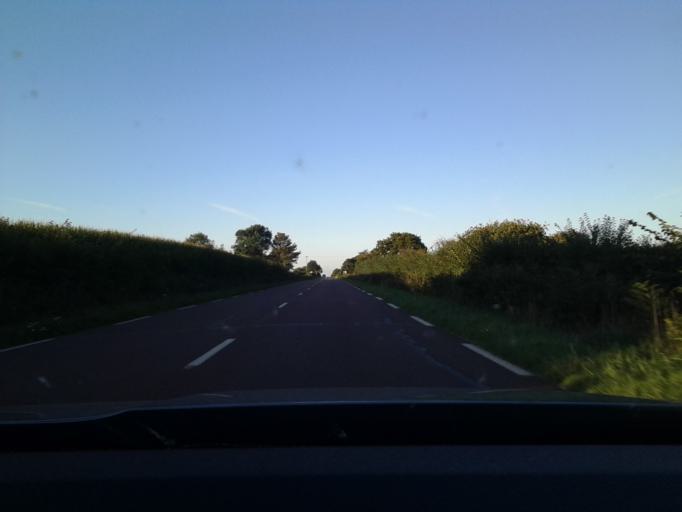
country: FR
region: Lower Normandy
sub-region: Departement de la Manche
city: Valognes
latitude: 49.4617
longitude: -1.4891
